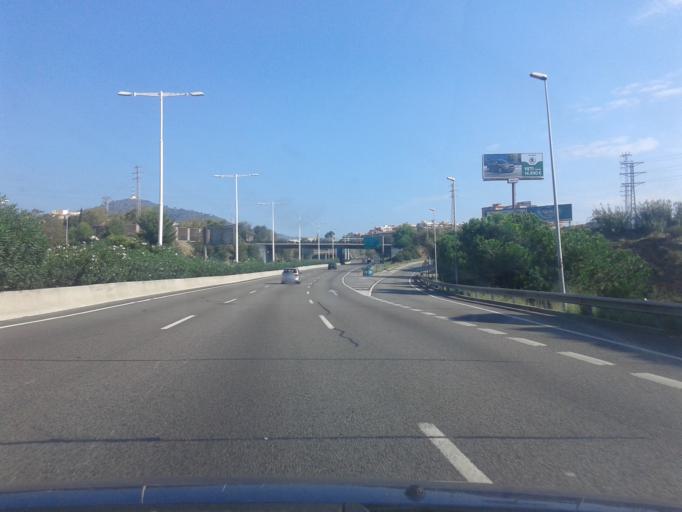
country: ES
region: Catalonia
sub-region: Provincia de Barcelona
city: Esplugues de Llobregat
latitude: 41.3684
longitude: 2.0911
